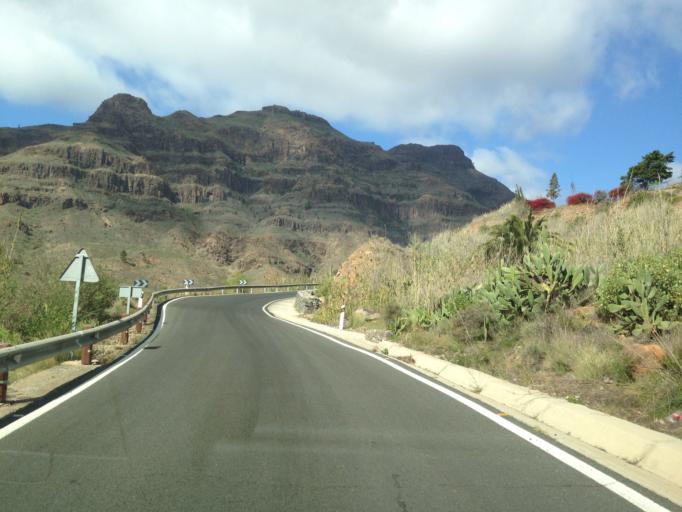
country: ES
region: Canary Islands
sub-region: Provincia de Las Palmas
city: Santa Lucia
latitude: 27.8725
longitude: -15.5641
